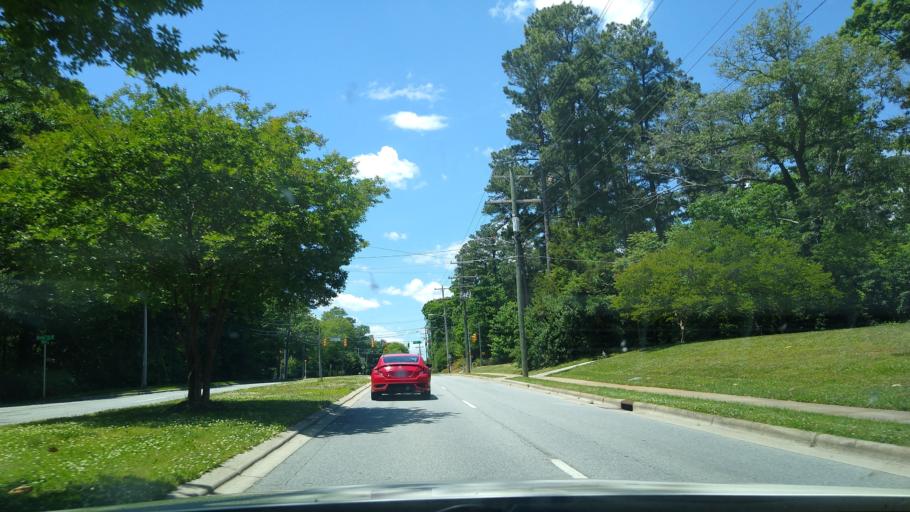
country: US
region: North Carolina
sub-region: Guilford County
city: Greensboro
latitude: 36.0907
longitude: -79.8573
